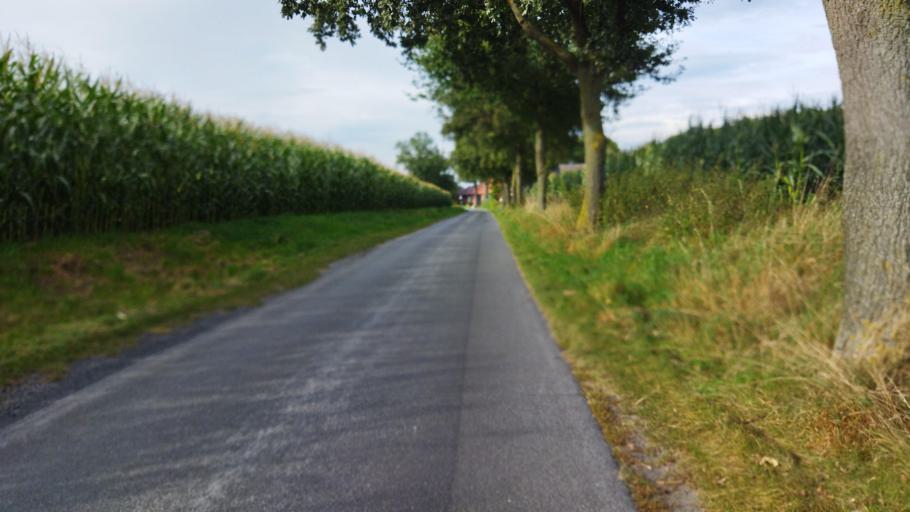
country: DE
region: North Rhine-Westphalia
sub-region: Regierungsbezirk Munster
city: Telgte
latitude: 52.0289
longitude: 7.7999
